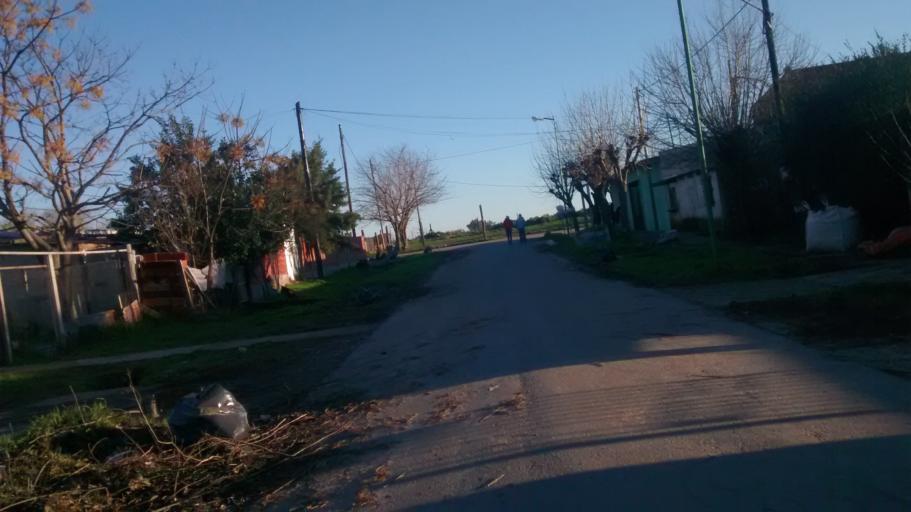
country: AR
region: Buenos Aires
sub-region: Partido de La Plata
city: La Plata
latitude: -34.9636
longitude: -57.9342
